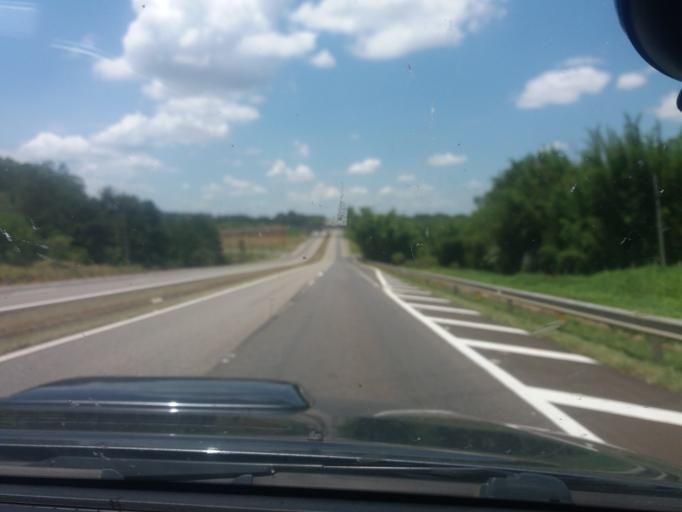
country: BR
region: Sao Paulo
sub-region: Itapetininga
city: Itapetininga
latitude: -23.5662
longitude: -47.9756
